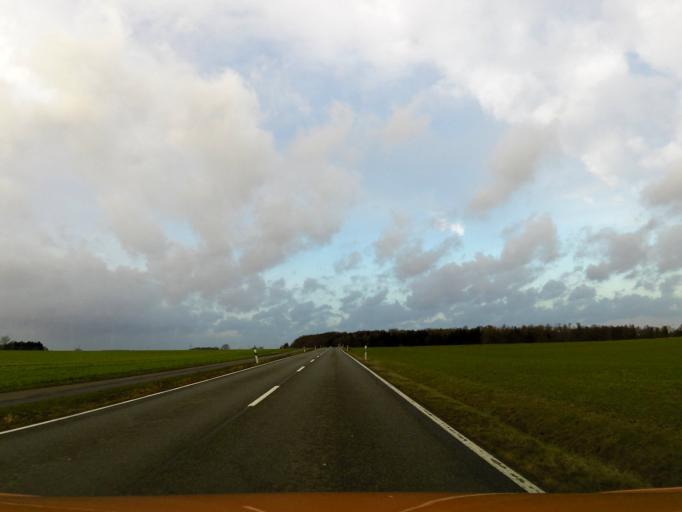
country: DE
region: Lower Saxony
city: Querenhorst
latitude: 52.3432
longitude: 10.9547
